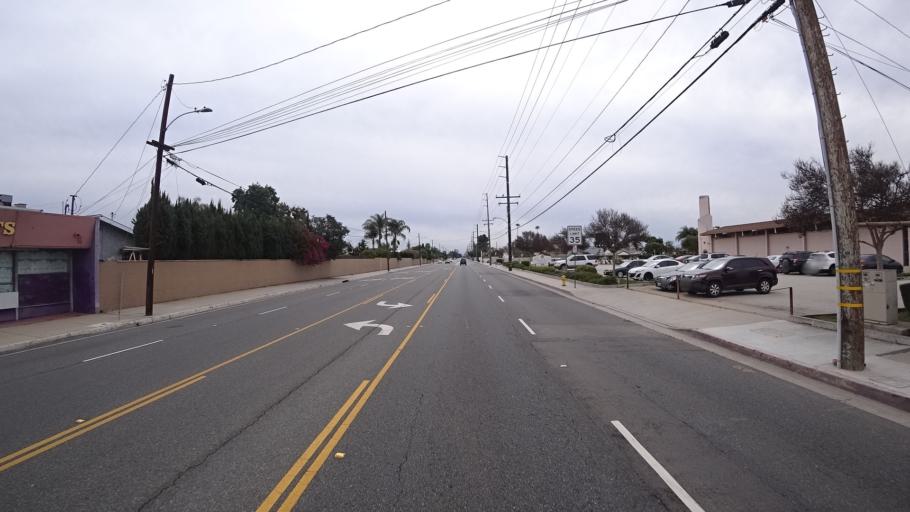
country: US
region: California
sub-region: Los Angeles County
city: West Puente Valley
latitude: 34.0604
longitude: -117.9631
